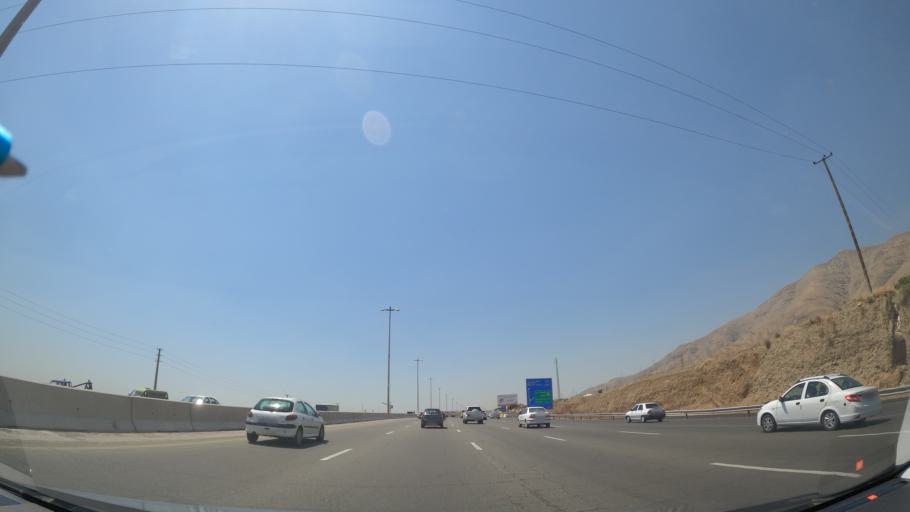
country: IR
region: Tehran
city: Shahr-e Qods
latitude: 35.7478
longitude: 51.0852
